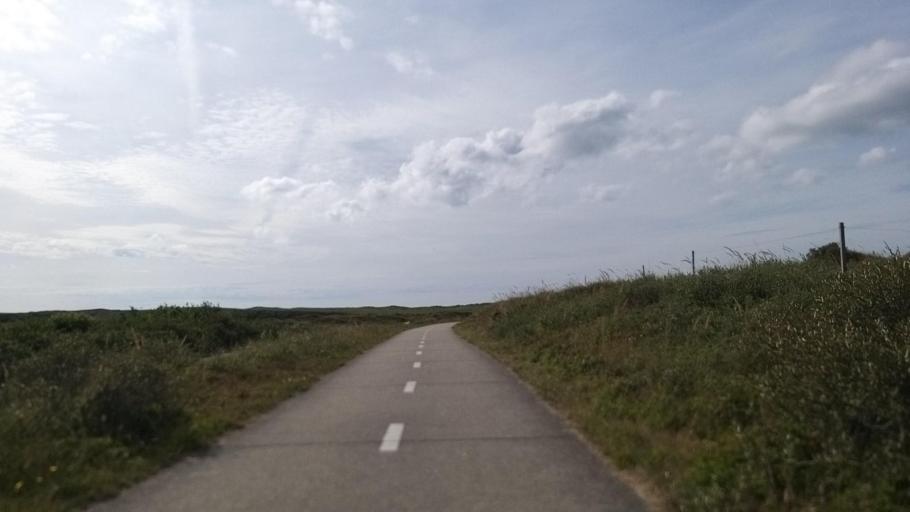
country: NL
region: North Holland
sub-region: Gemeente Texel
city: Den Burg
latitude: 53.1598
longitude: 4.8267
